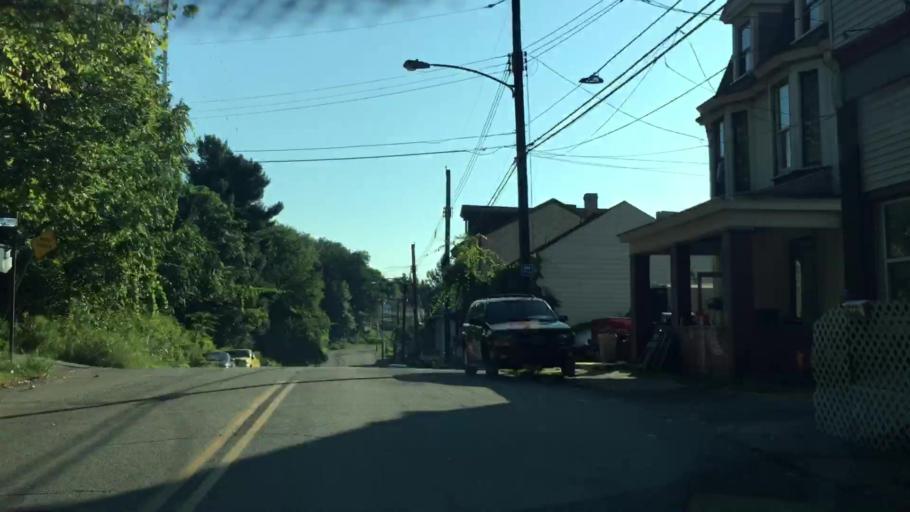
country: US
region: Pennsylvania
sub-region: Allegheny County
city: Millvale
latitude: 40.4696
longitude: -79.9990
